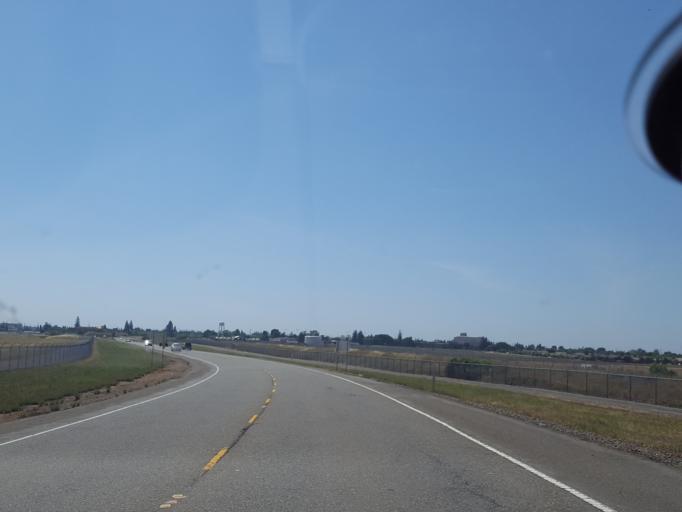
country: US
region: California
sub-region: Sacramento County
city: Rancho Cordova
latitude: 38.5675
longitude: -121.2751
